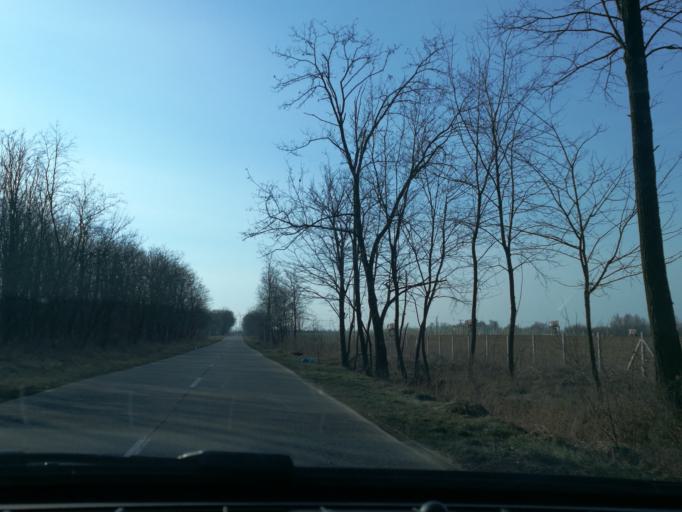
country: HU
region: Szabolcs-Szatmar-Bereg
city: Levelek
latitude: 47.9871
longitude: 21.9688
